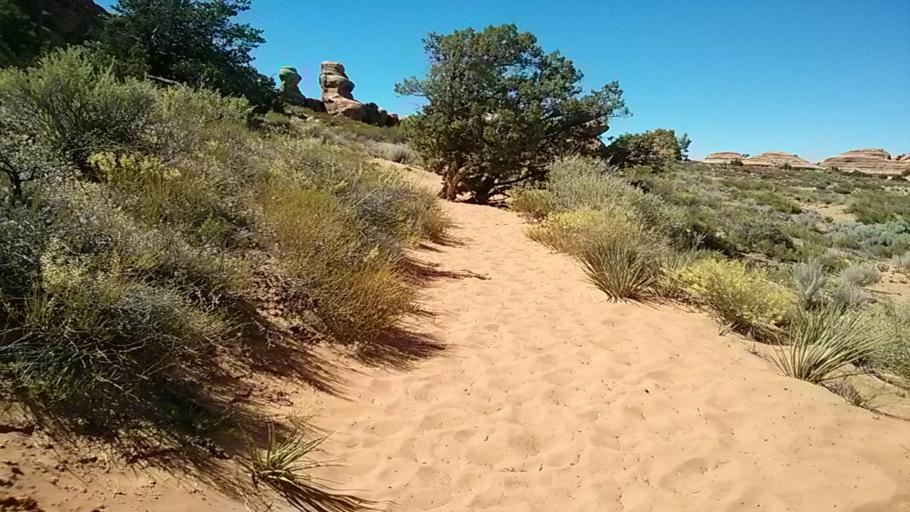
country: US
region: Utah
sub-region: Grand County
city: Moab
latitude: 38.7908
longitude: -109.6044
